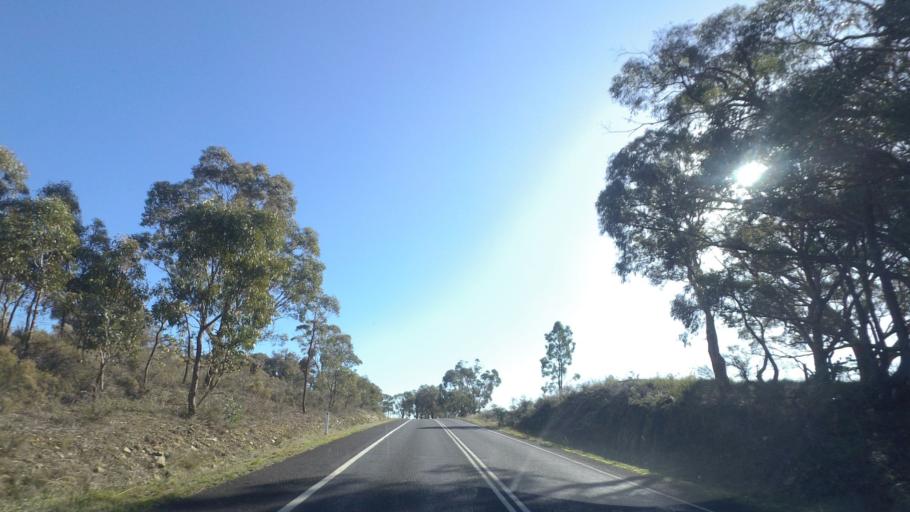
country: AU
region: Victoria
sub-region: Greater Bendigo
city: Kennington
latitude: -36.9114
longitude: 144.3266
